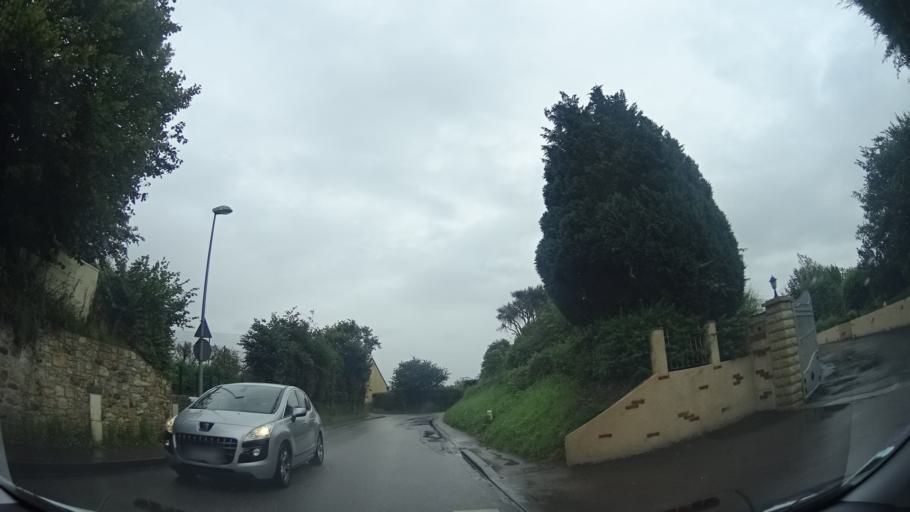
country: FR
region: Lower Normandy
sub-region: Departement de la Manche
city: Urville-Nacqueville
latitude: 49.5948
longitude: -1.7711
